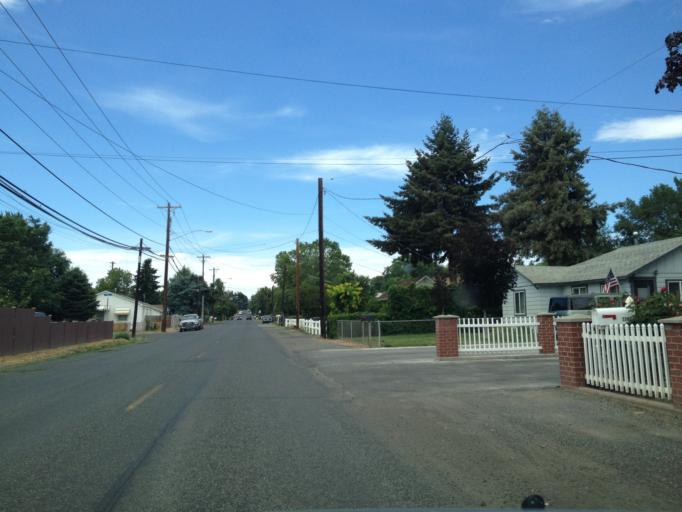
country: US
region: Washington
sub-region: Yakima County
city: Yakima
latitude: 46.6071
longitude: -120.5402
